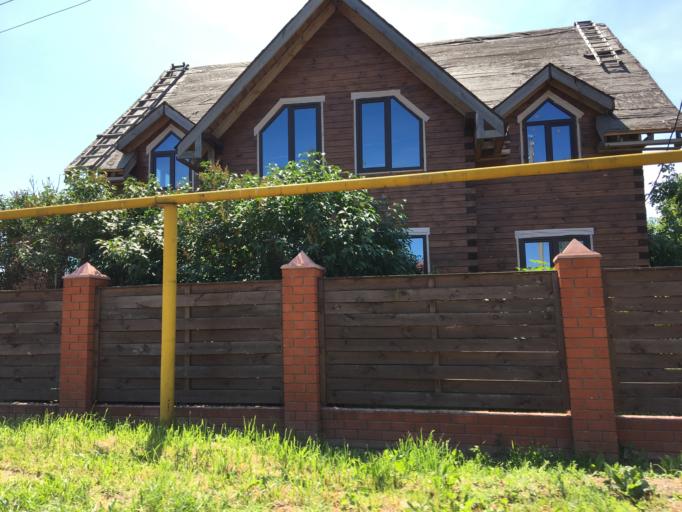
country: RU
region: Nizjnij Novgorod
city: Spasskoye
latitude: 56.1076
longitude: 45.5015
